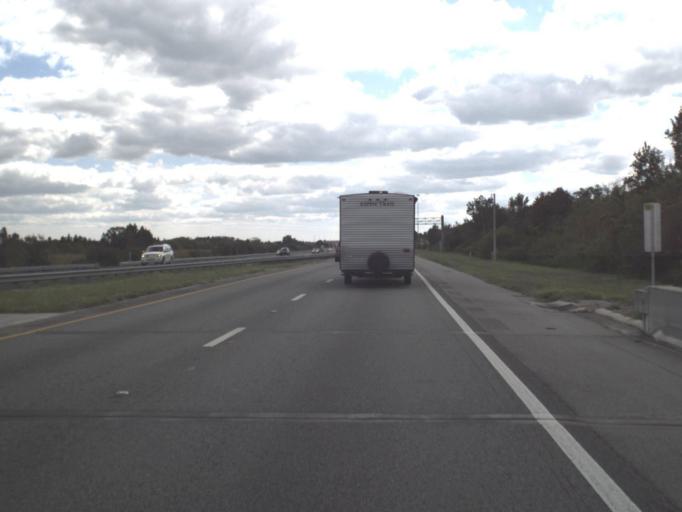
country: US
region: Florida
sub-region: Osceola County
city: Saint Cloud
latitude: 28.1910
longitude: -81.3050
